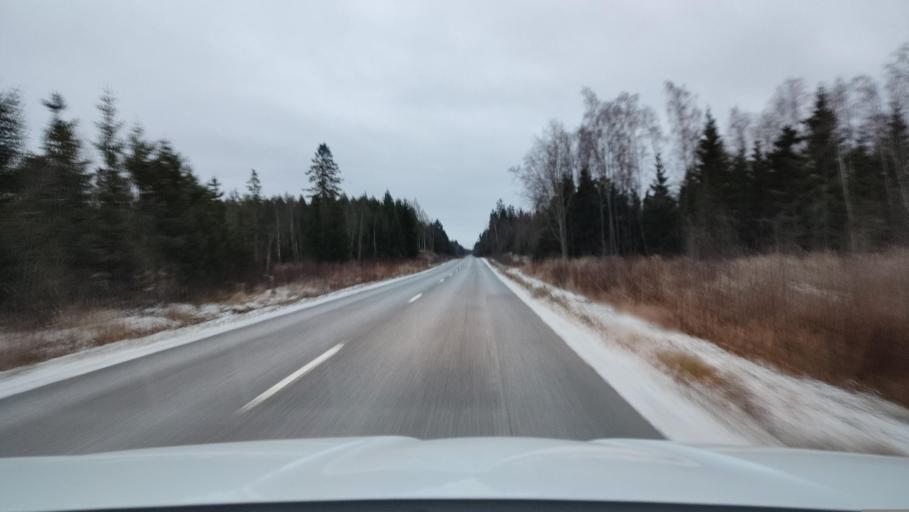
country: FI
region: Ostrobothnia
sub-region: Vaasa
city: Replot
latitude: 63.2584
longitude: 21.3650
